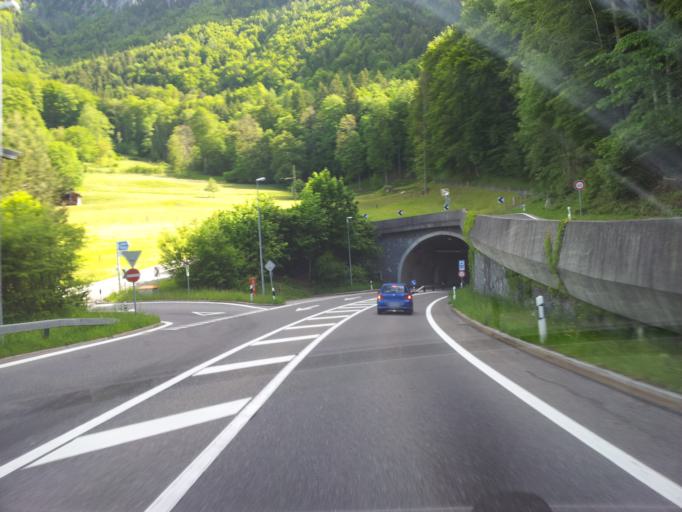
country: CH
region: Obwalden
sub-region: Obwalden
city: Lungern
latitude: 46.7510
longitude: 8.1076
